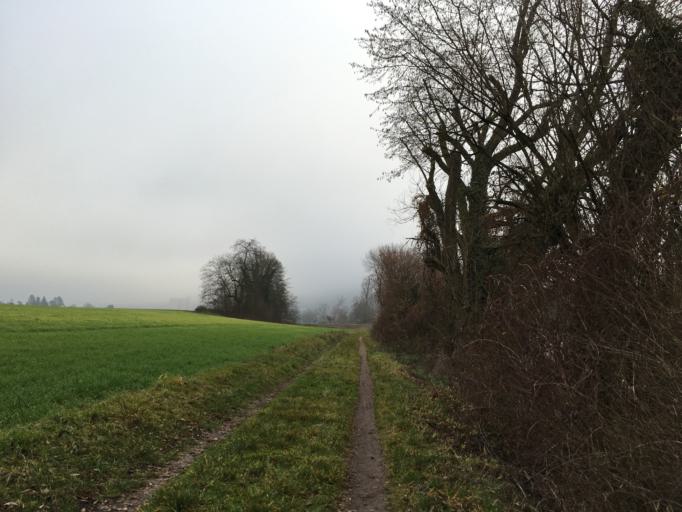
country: CH
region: Aargau
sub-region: Bezirk Zurzach
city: Bad Zurzach
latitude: 47.5776
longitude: 8.3191
